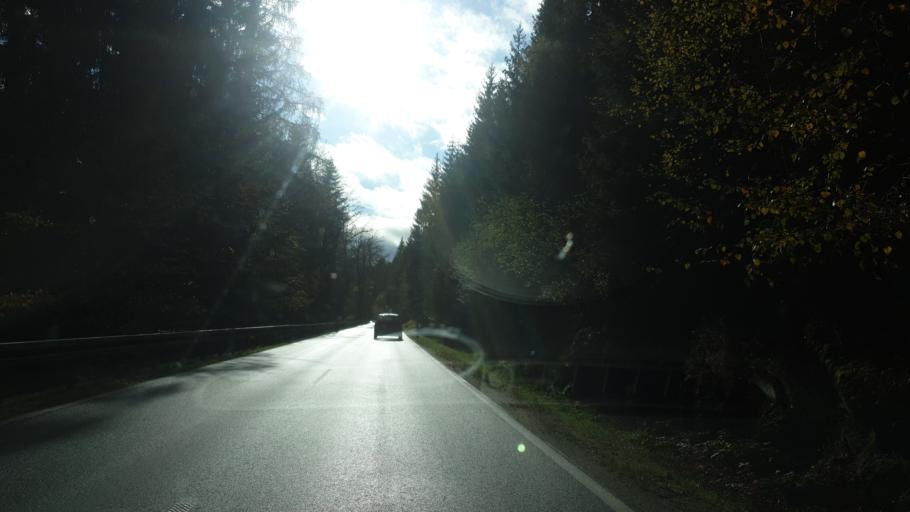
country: DE
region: Saxony
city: Zschorlau
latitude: 50.5367
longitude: 12.6529
